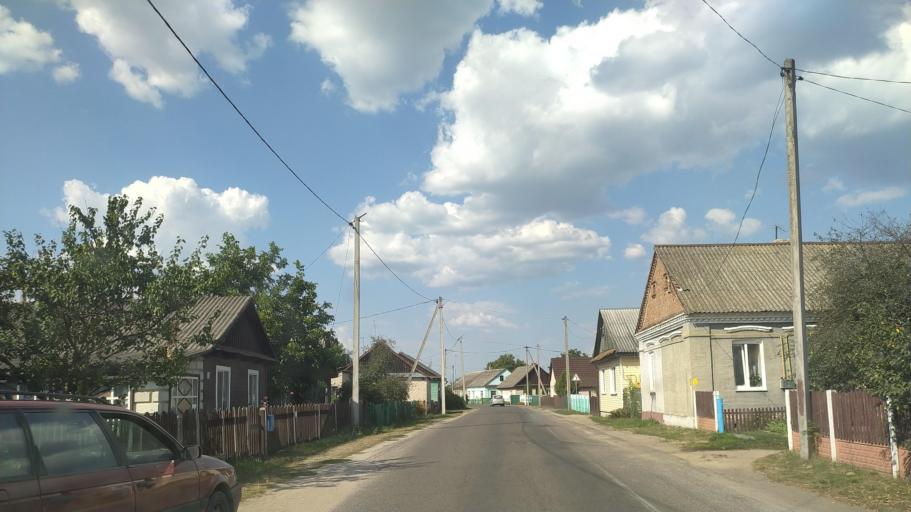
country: BY
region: Brest
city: Drahichyn
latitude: 52.1878
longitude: 25.1477
